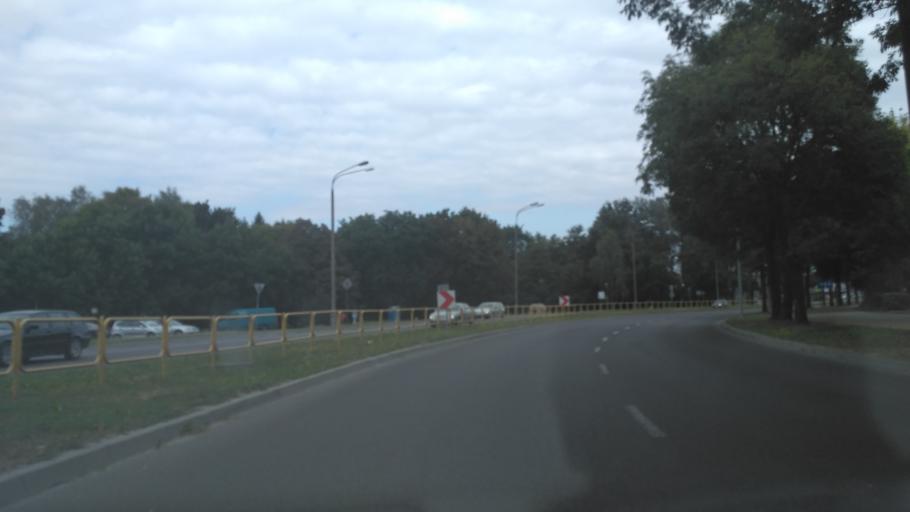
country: PL
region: Lublin Voivodeship
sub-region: Chelm
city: Chelm
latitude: 51.1342
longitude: 23.4642
